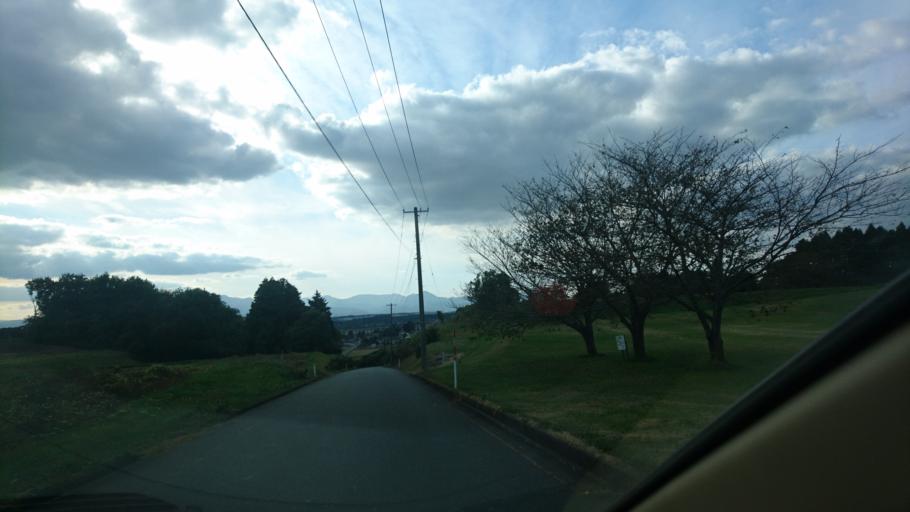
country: JP
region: Iwate
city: Kitakami
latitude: 39.2422
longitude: 141.1301
